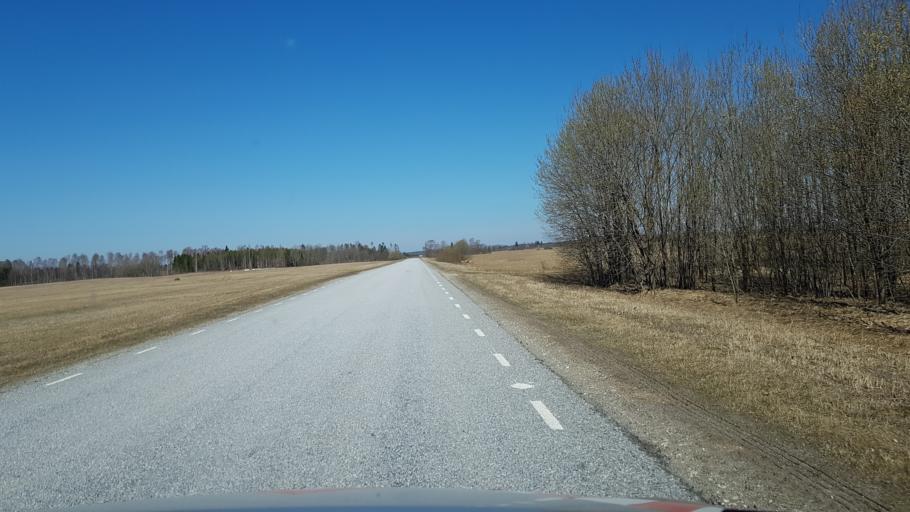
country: EE
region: Jaervamaa
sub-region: Koeru vald
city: Koeru
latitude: 59.0172
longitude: 26.0883
